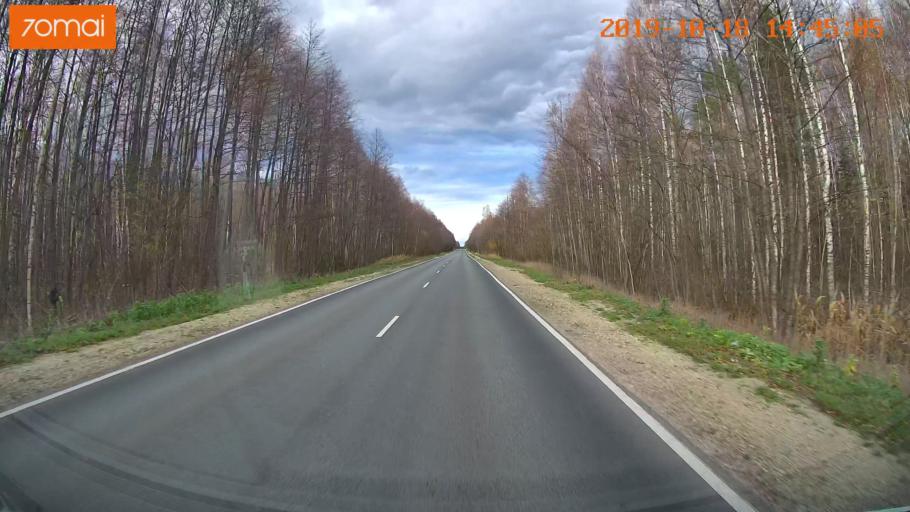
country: RU
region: Vladimir
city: Velikodvorskiy
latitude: 55.3490
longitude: 40.6782
